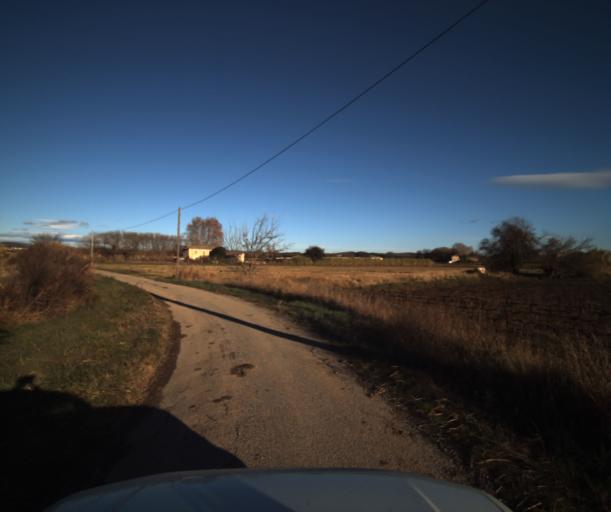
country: FR
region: Provence-Alpes-Cote d'Azur
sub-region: Departement du Vaucluse
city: Pertuis
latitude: 43.6829
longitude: 5.4762
